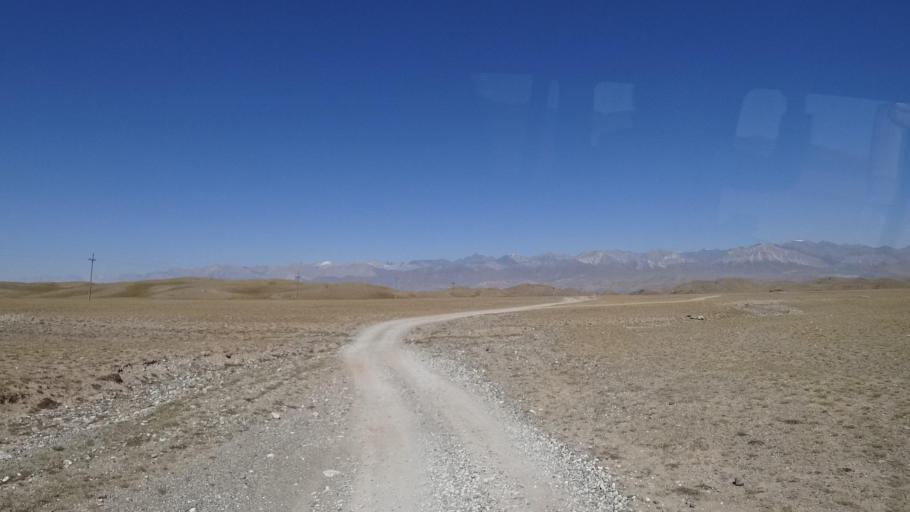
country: KG
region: Osh
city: Gul'cha
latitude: 39.5798
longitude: 72.8916
